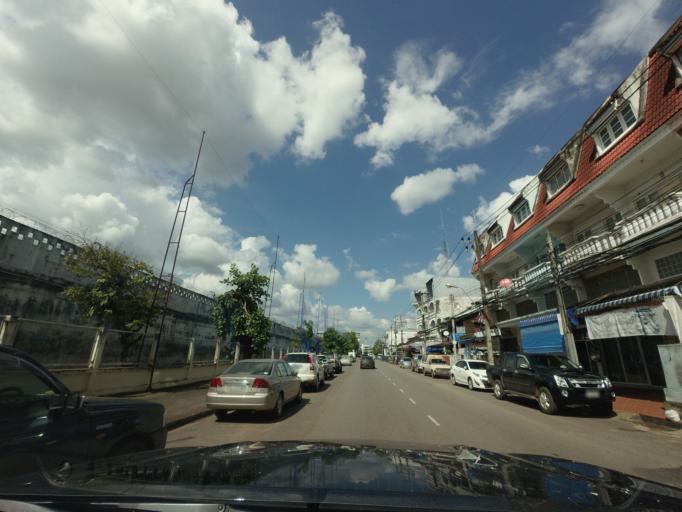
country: TH
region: Changwat Udon Thani
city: Udon Thani
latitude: 17.4035
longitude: 102.7858
